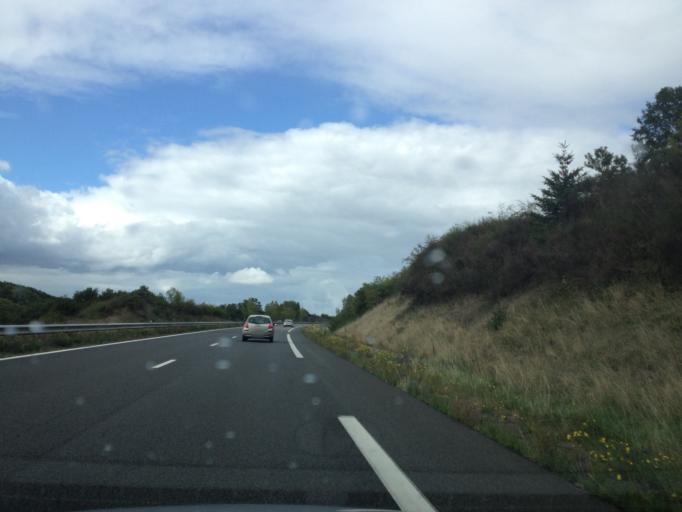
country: FR
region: Rhone-Alpes
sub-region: Departement de la Loire
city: Commelle-Vernay
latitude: 45.9788
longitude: 4.1222
